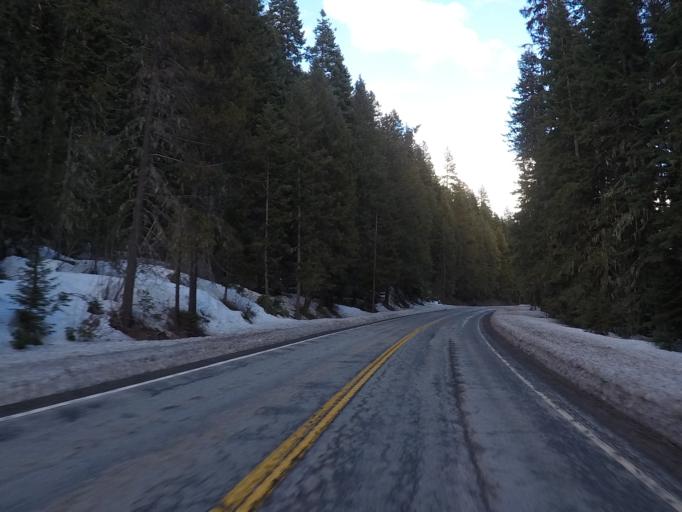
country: US
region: Montana
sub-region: Ravalli County
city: Hamilton
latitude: 46.5164
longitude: -114.7570
